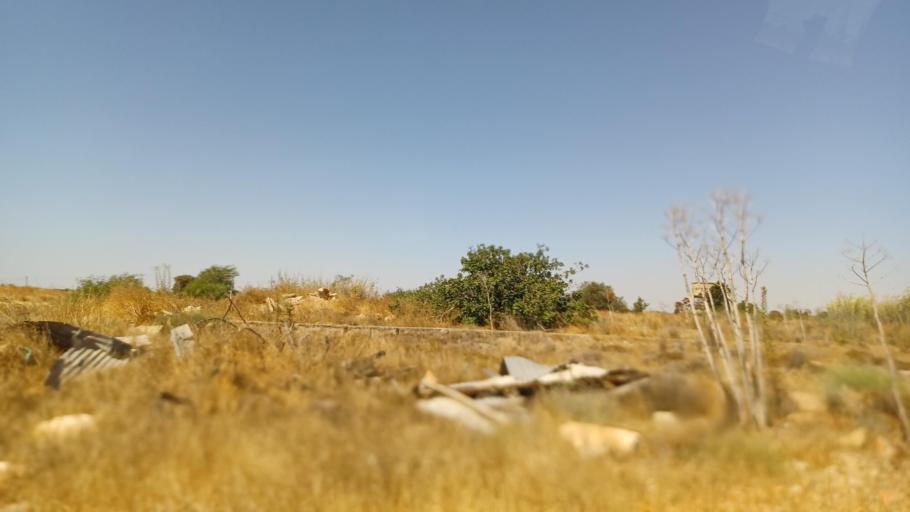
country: CY
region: Larnaka
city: Pergamos
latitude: 35.0248
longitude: 33.7155
